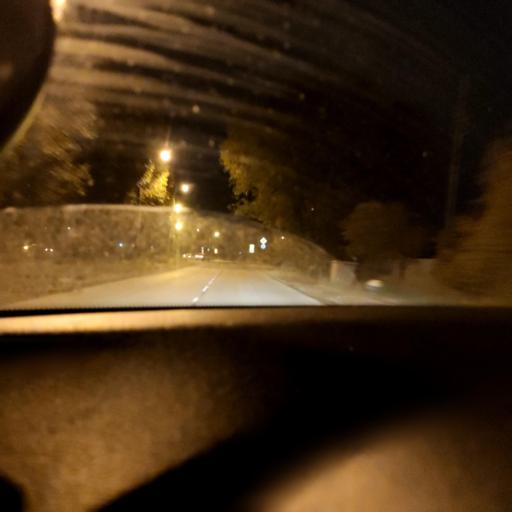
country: RU
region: Samara
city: Smyshlyayevka
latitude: 53.2339
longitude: 50.3070
